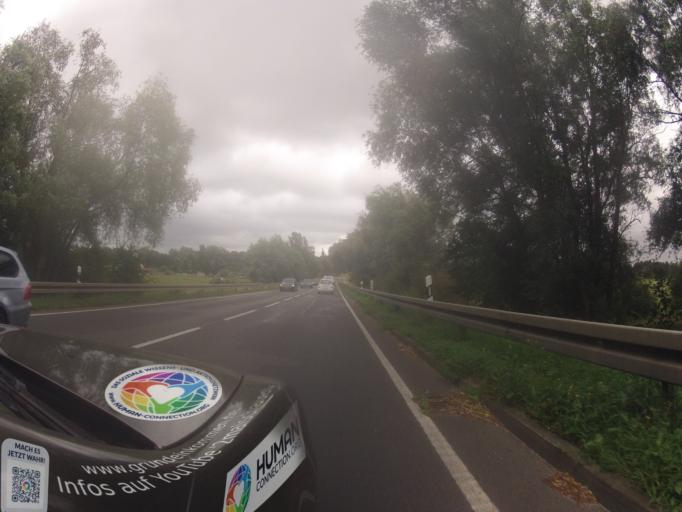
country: DE
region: Mecklenburg-Vorpommern
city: Pasewalk
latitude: 53.5029
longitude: 13.9807
